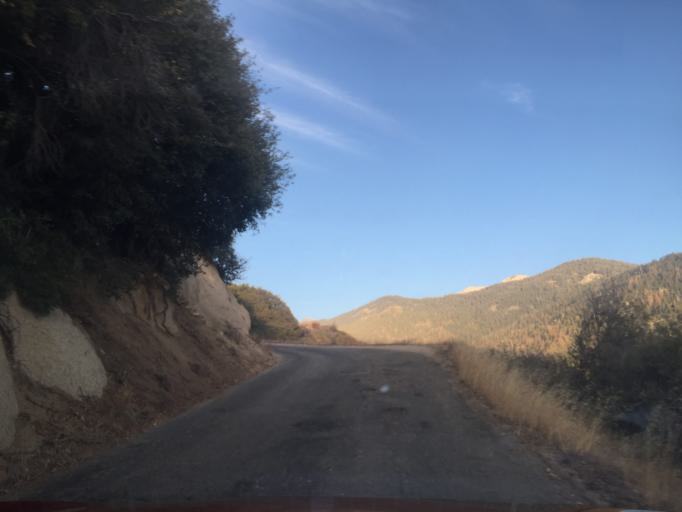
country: US
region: California
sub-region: Tulare County
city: Three Rivers
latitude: 36.4362
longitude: -118.7247
